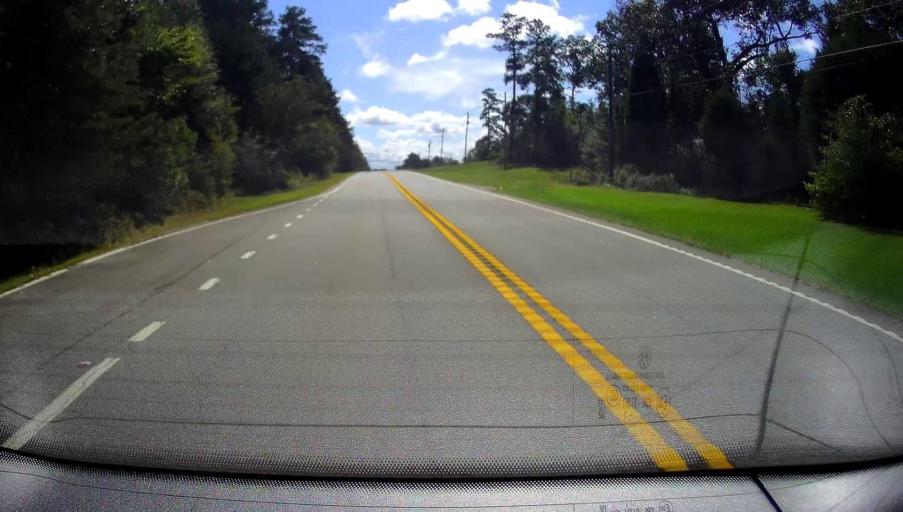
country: US
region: Georgia
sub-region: Bibb County
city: Macon
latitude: 32.8317
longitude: -83.5742
